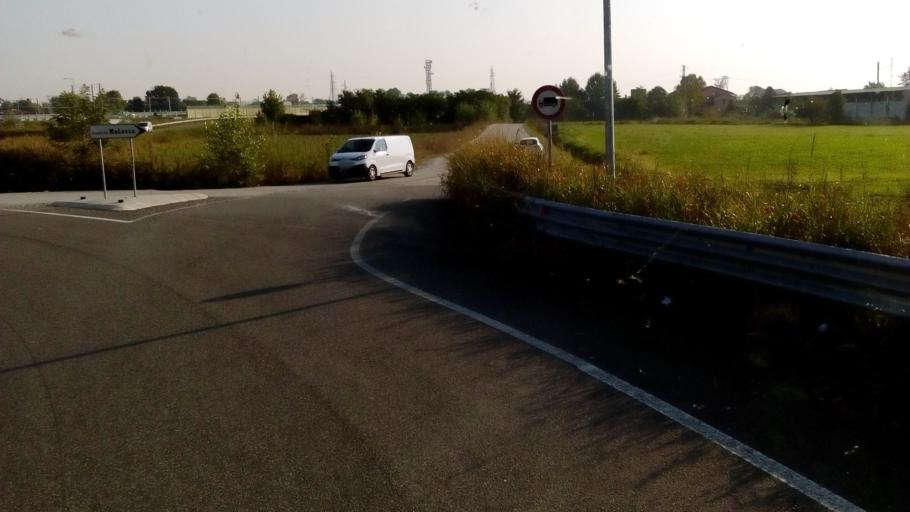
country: IT
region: Lombardy
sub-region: Provincia di Bergamo
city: Casirate d'Adda
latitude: 45.5058
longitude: 9.5568
